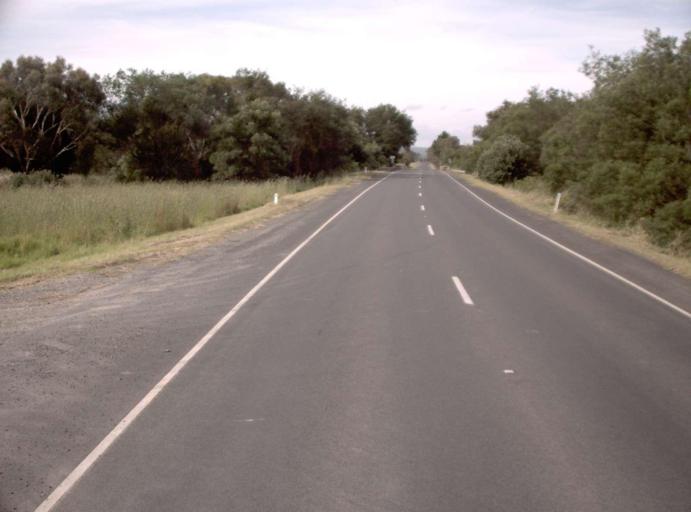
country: AU
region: Victoria
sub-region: Latrobe
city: Traralgon
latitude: -38.1548
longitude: 146.5537
